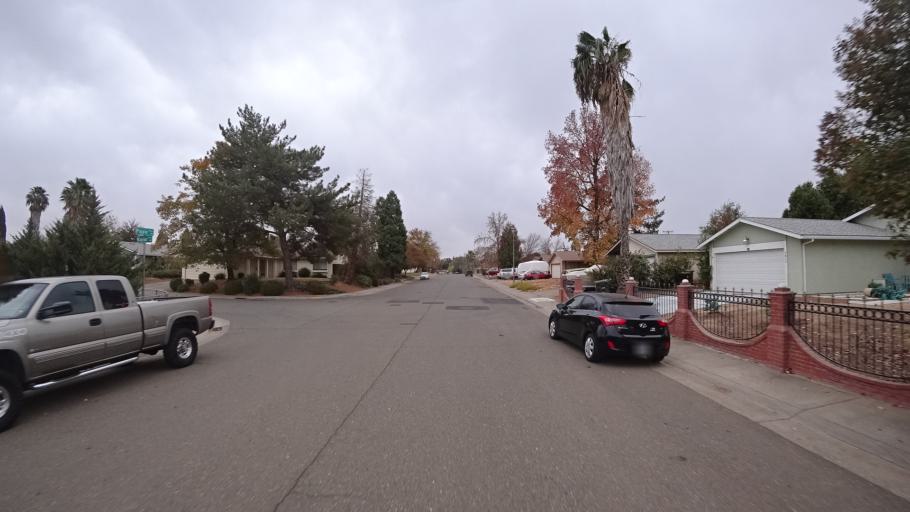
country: US
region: California
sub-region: Sacramento County
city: Citrus Heights
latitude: 38.6939
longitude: -121.3040
